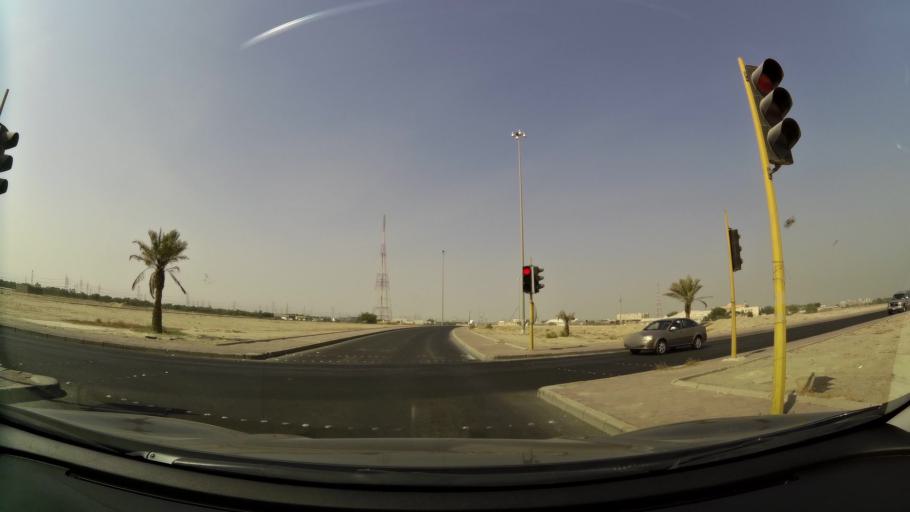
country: KW
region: Al Ahmadi
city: Al Fahahil
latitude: 29.0749
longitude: 48.1094
